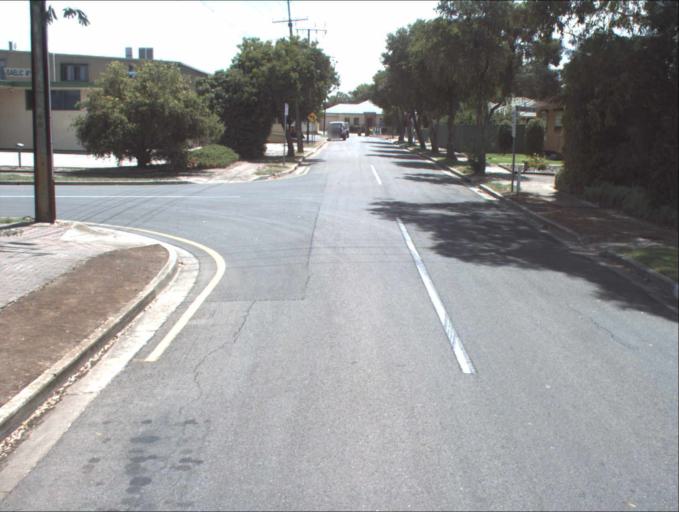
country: AU
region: South Australia
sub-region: Port Adelaide Enfield
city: Gilles Plains
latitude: -34.8570
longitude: 138.6616
